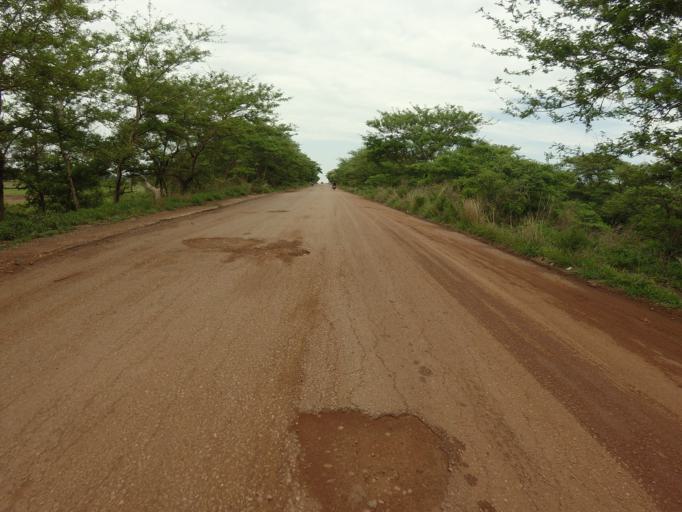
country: GH
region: Upper East
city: Bawku
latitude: 11.0027
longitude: -0.3881
